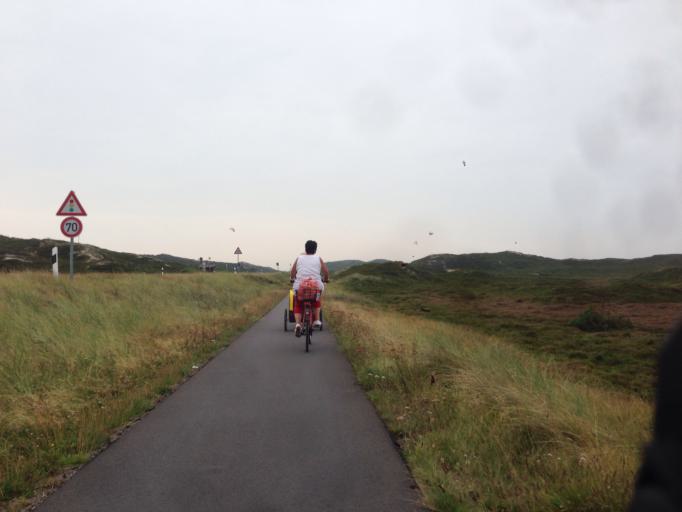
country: DE
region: Schleswig-Holstein
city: Westerland
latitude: 54.8019
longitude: 8.2881
